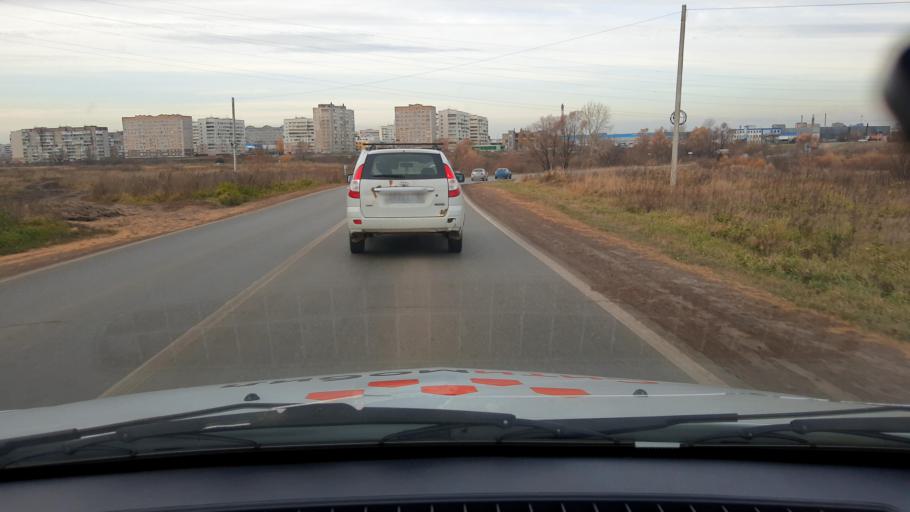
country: RU
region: Bashkortostan
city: Iglino
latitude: 54.7503
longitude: 56.2503
